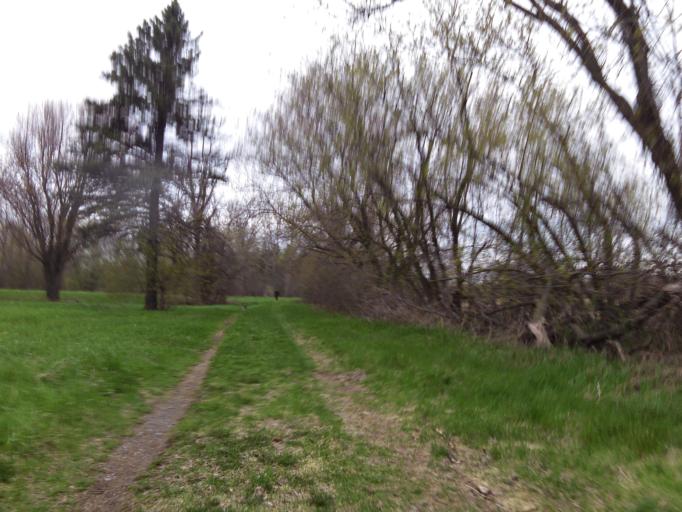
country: CA
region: Ontario
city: Ottawa
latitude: 45.4175
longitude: -75.5918
